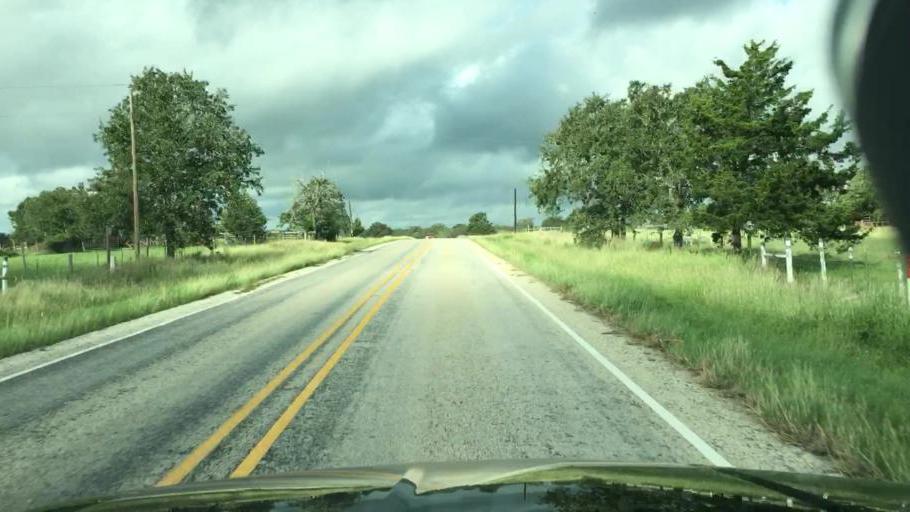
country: US
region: Texas
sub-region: Lee County
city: Giddings
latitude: 30.2717
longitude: -96.8086
